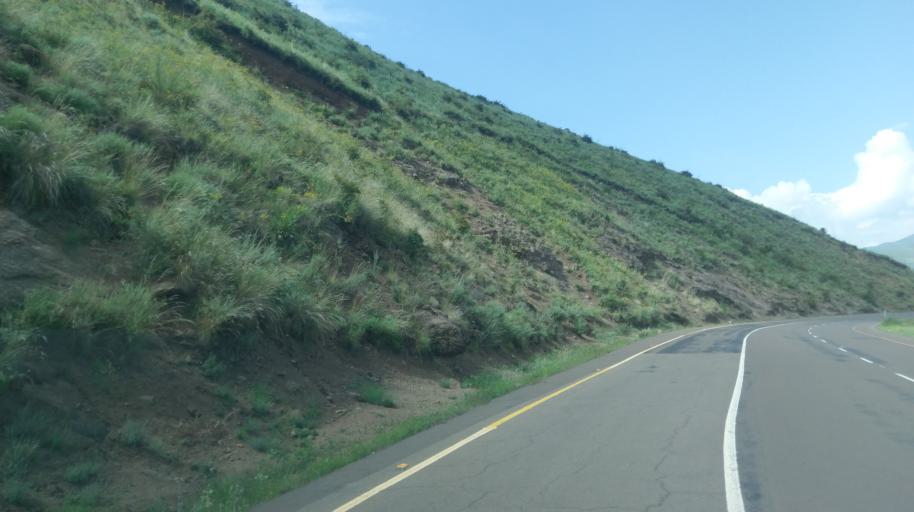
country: LS
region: Thaba-Tseka
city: Thaba-Tseka
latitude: -29.1493
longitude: 28.4855
